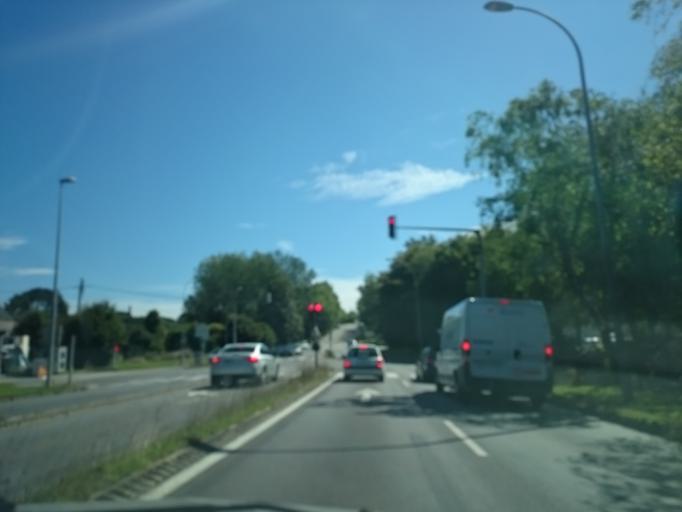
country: FR
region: Brittany
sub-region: Departement du Finistere
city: Bohars
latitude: 48.4101
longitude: -4.5226
